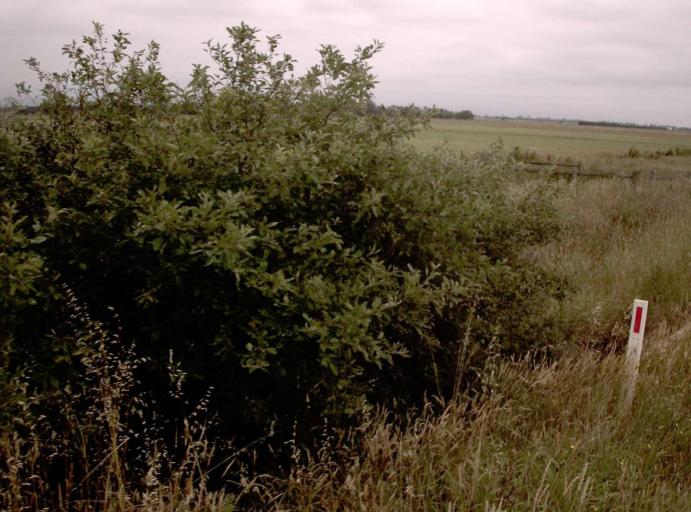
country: AU
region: Victoria
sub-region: Wellington
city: Heyfield
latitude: -38.1006
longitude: 146.7733
